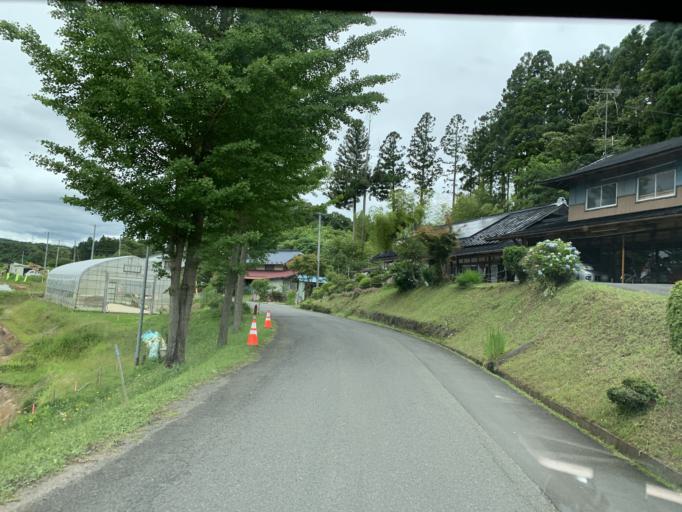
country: JP
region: Iwate
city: Ichinoseki
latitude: 38.9132
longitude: 141.0185
